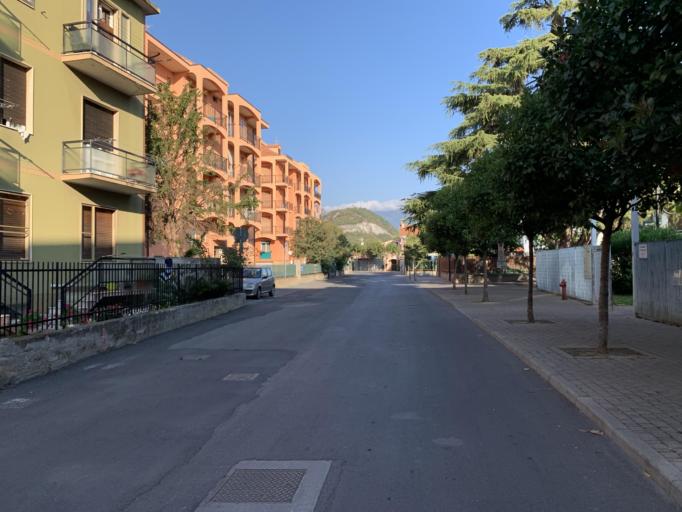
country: IT
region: Liguria
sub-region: Provincia di Savona
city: Pietra Ligure
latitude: 44.1561
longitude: 8.2867
